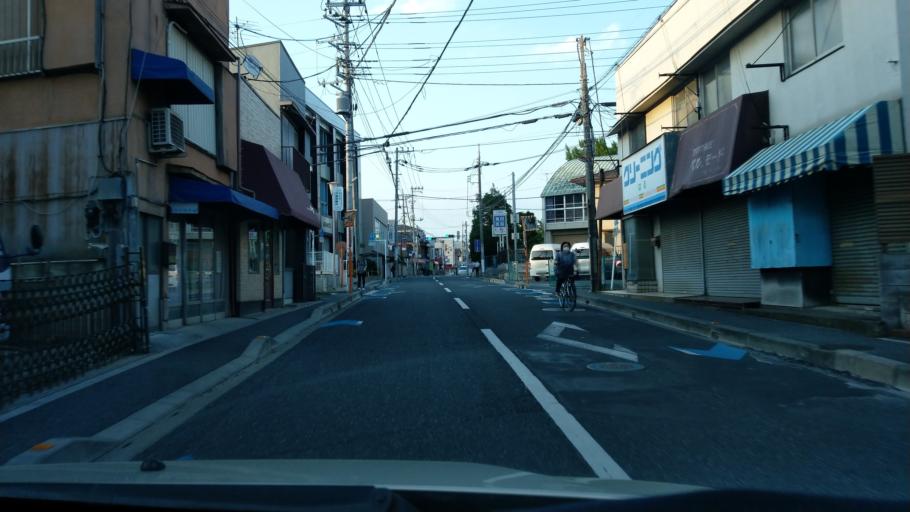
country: JP
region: Saitama
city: Yono
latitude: 35.8773
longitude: 139.6502
